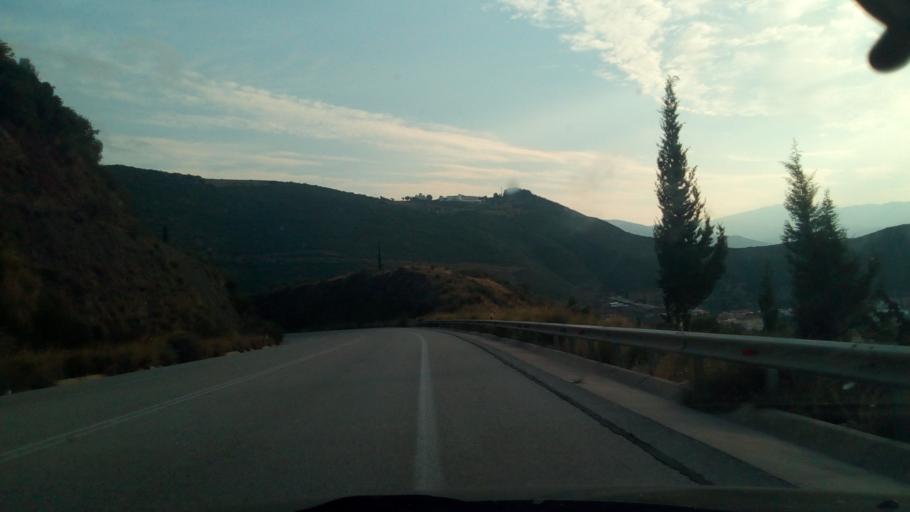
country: GR
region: West Greece
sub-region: Nomos Aitolias kai Akarnanias
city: Nafpaktos
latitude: 38.4076
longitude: 21.8389
